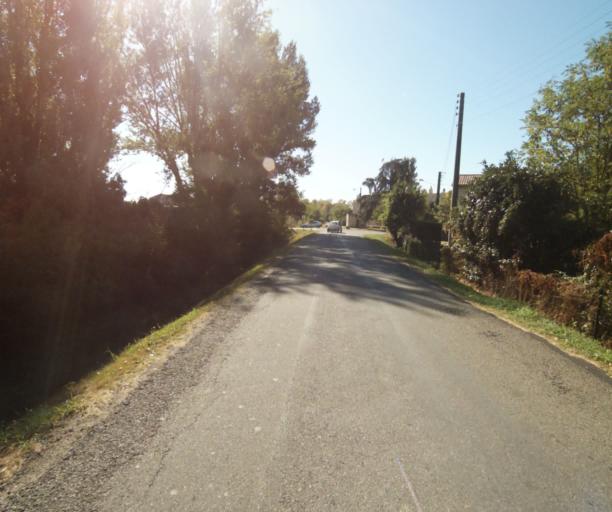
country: FR
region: Midi-Pyrenees
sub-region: Departement du Tarn-et-Garonne
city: Moissac
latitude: 44.1006
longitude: 1.1022
